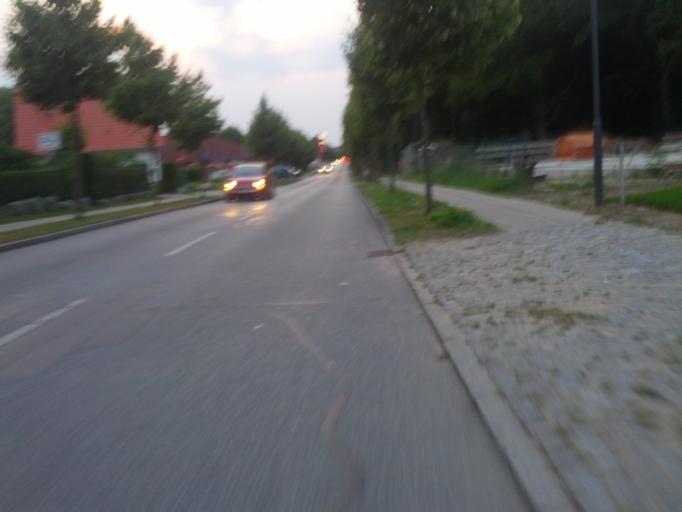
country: DE
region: Mecklenburg-Vorpommern
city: Ostseebad Kuhlungsborn
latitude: 54.1440
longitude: 11.7382
